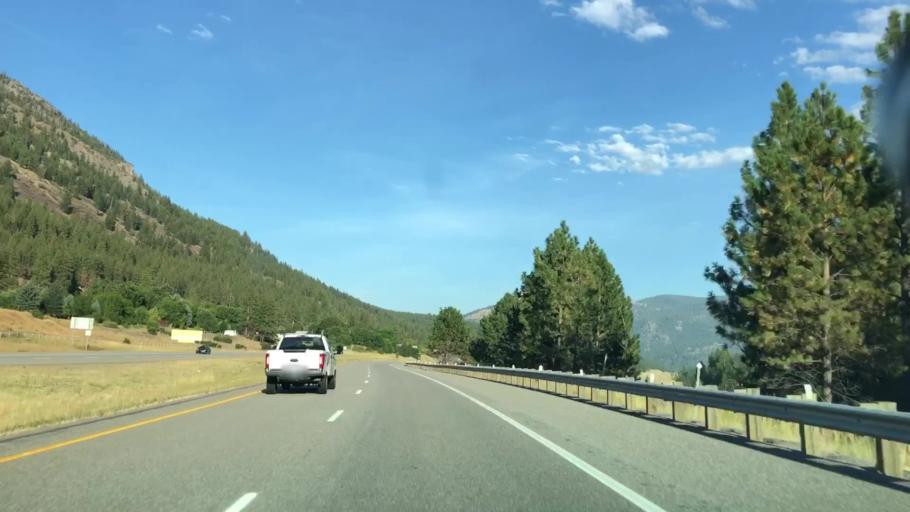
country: US
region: Montana
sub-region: Missoula County
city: Frenchtown
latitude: 47.0007
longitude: -114.4803
